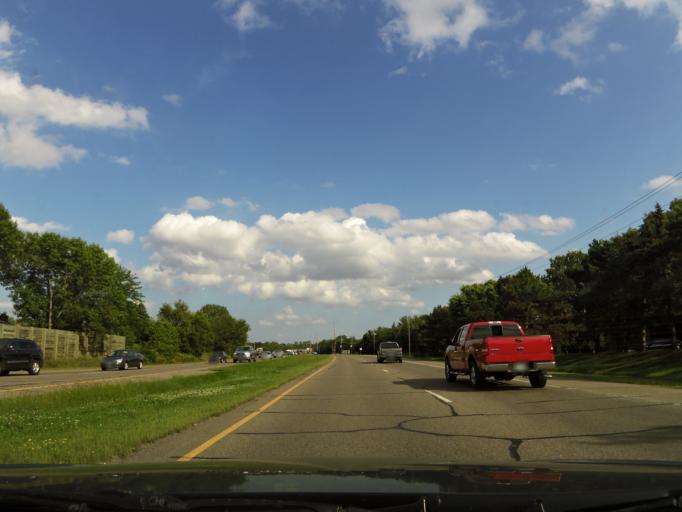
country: US
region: Minnesota
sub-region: Dakota County
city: Burnsville
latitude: 44.7390
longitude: -93.2669
